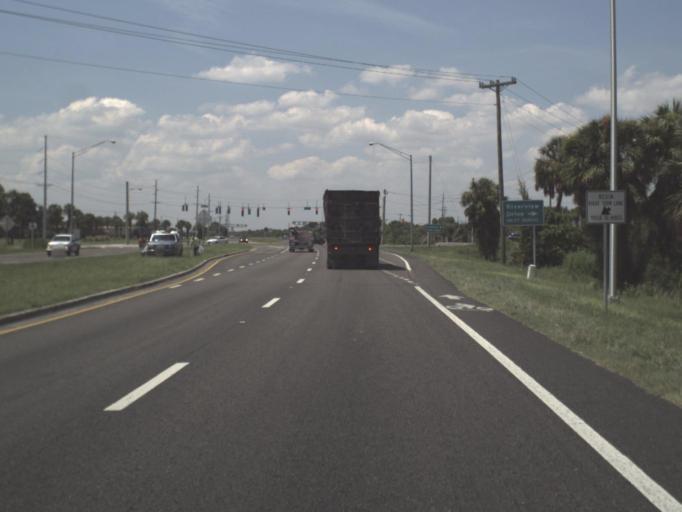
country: US
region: Florida
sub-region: Hillsborough County
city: Gibsonton
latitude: 27.8630
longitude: -82.3845
